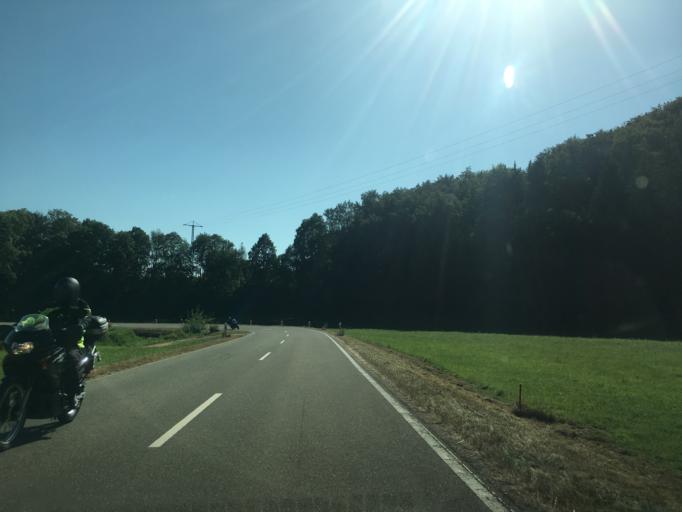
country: DE
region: Baden-Wuerttemberg
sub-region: Tuebingen Region
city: Hayingen
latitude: 48.2983
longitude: 9.4914
